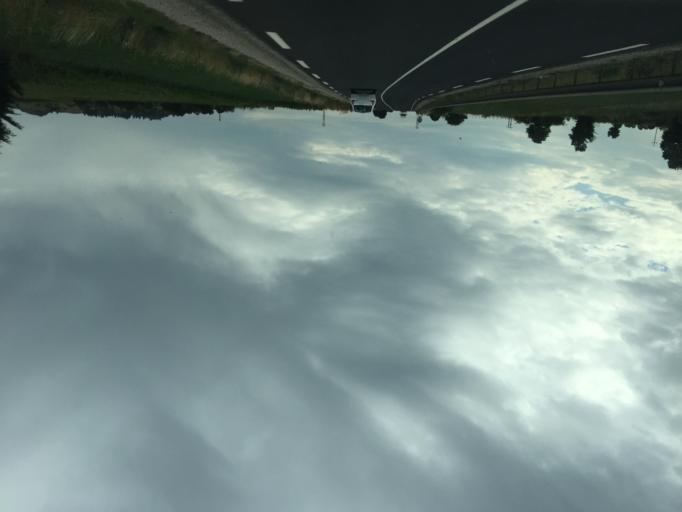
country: FR
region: Auvergne
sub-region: Departement de la Haute-Loire
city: Solignac-sur-Loire
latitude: 44.8773
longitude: 3.8469
